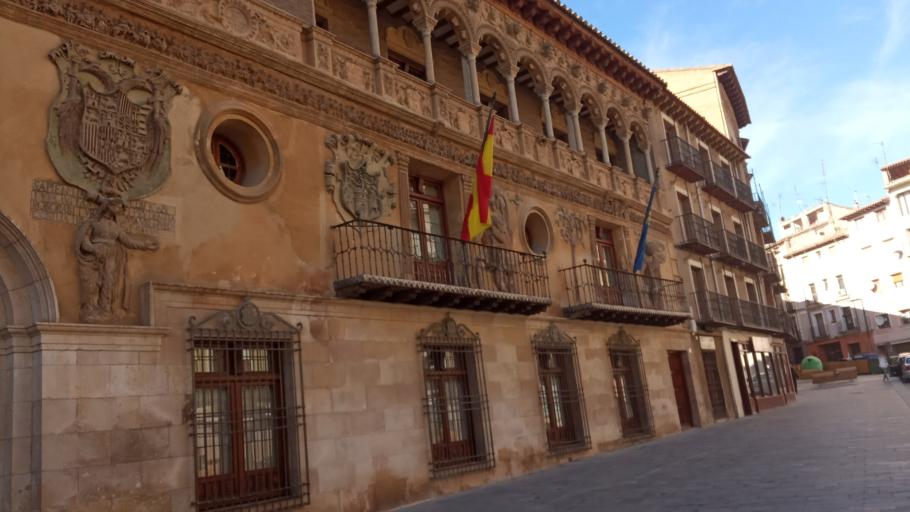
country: ES
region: Aragon
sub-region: Provincia de Zaragoza
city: Tarazona
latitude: 41.9053
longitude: -1.7271
